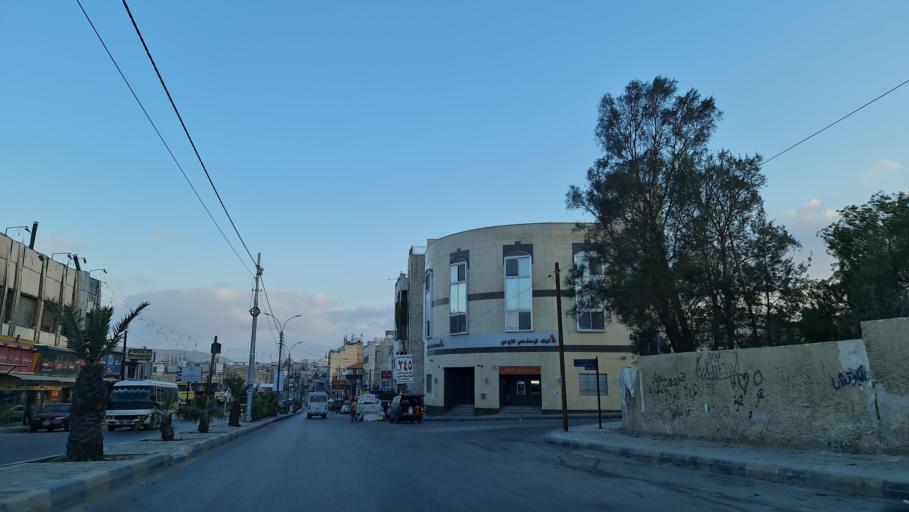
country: JO
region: Zarqa
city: Zarqa
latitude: 32.0753
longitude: 36.0779
